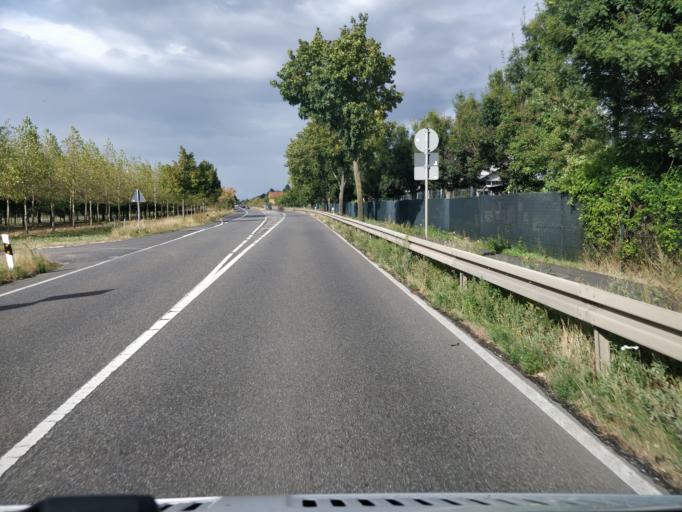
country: DE
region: North Rhine-Westphalia
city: Meckenheim
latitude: 50.6377
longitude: 7.0338
